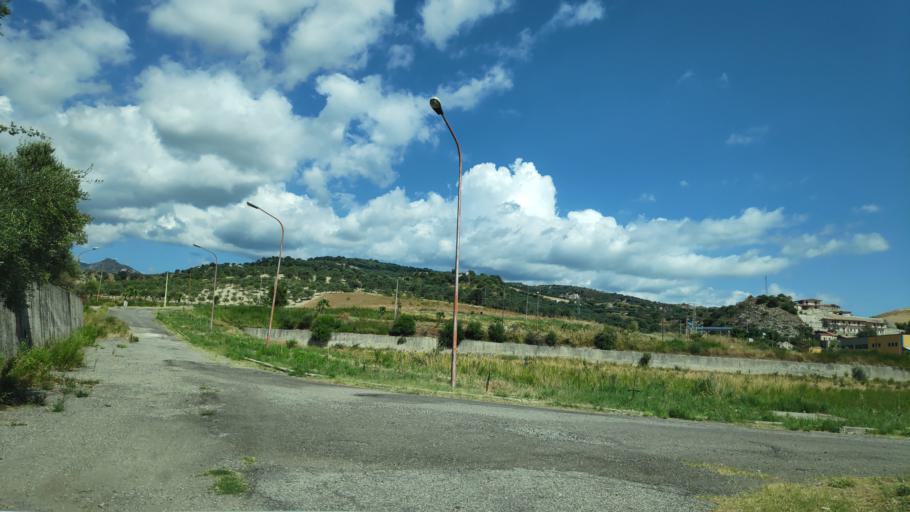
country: IT
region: Calabria
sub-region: Provincia di Reggio Calabria
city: Camini
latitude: 38.4632
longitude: 16.5023
